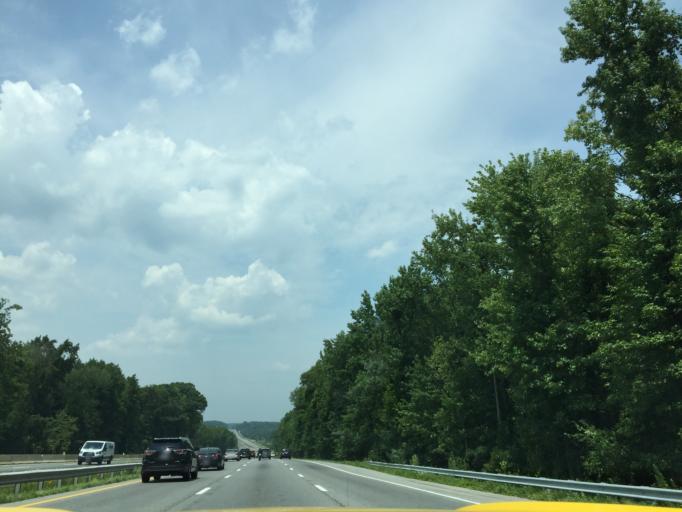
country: US
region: Maryland
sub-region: Prince George's County
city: Fort Washington
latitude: 38.7177
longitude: -76.9898
